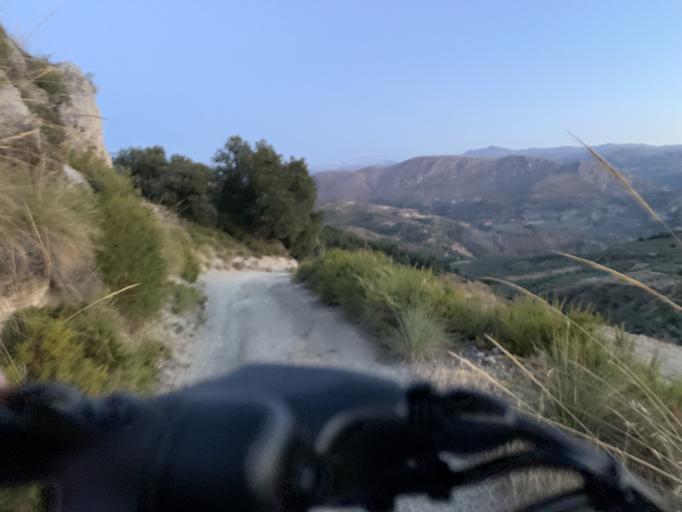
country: ES
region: Andalusia
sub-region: Provincia de Granada
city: Beas de Granada
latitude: 37.2201
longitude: -3.4521
